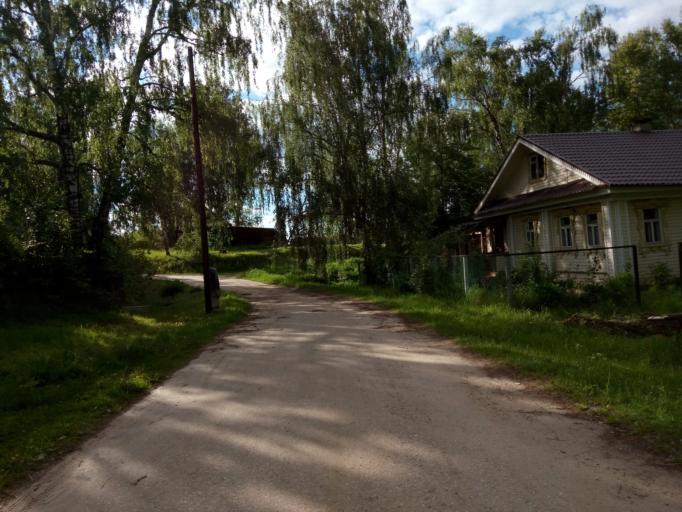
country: RU
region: Nizjnij Novgorod
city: Voskresenskoye
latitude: 56.7850
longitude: 45.5170
